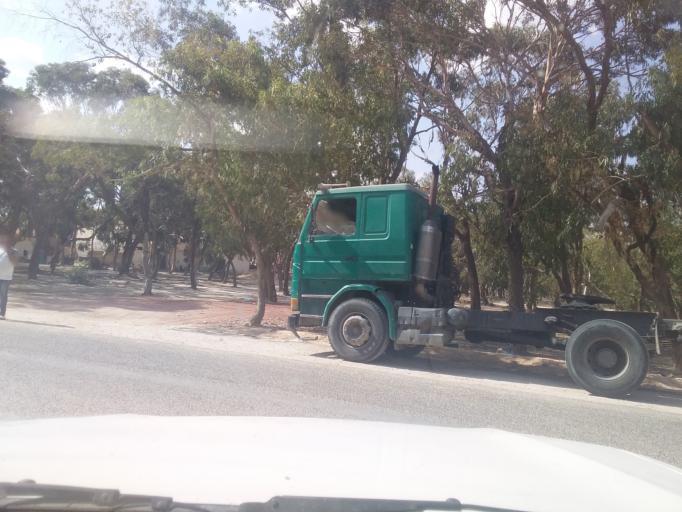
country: TN
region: Qabis
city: Gabes
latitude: 33.6226
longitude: 10.2790
